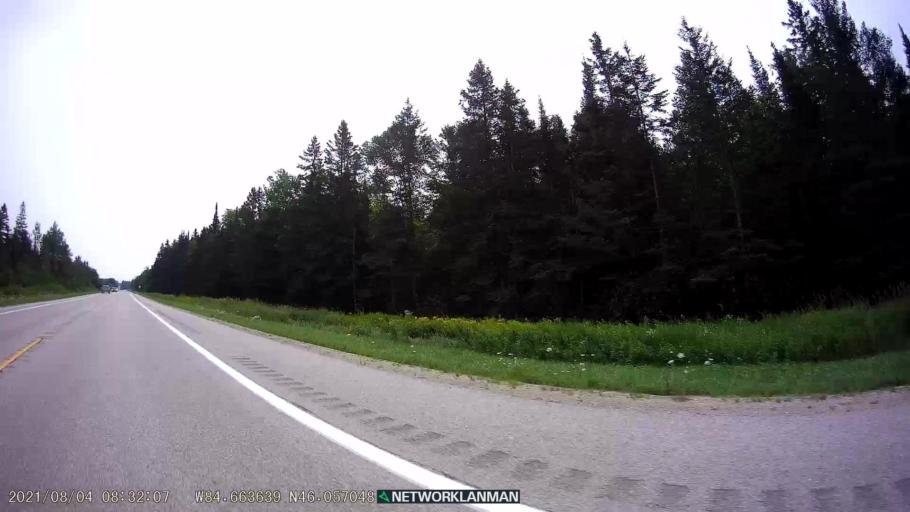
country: US
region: Michigan
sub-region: Mackinac County
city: Saint Ignace
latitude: 46.0570
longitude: -84.6631
